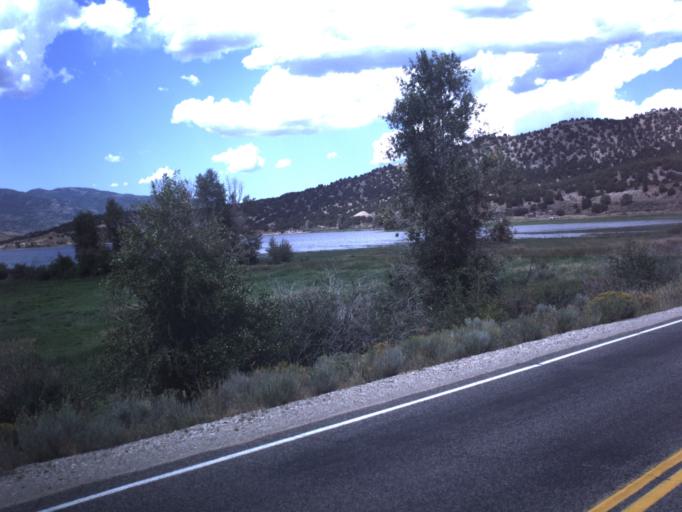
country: US
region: Utah
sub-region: Summit County
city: Oakley
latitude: 40.7535
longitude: -111.3756
